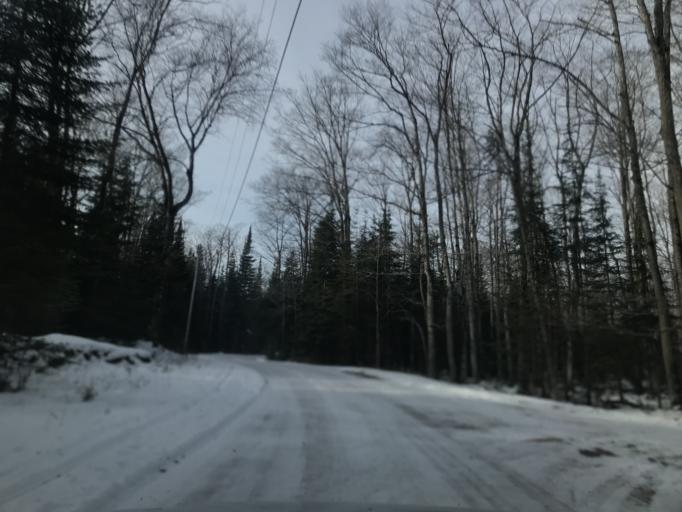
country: US
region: Wisconsin
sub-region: Door County
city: Sturgeon Bay
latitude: 45.1553
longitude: -87.0437
